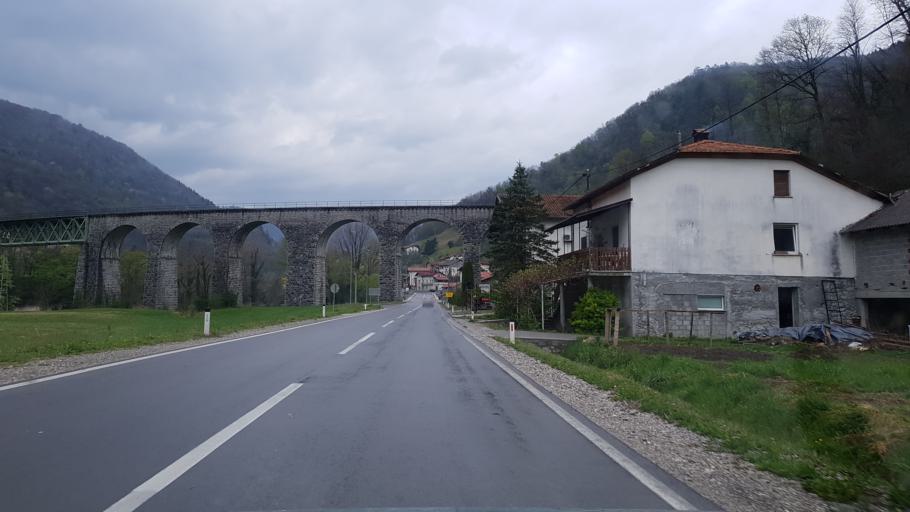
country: SI
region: Tolmin
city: Tolmin
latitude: 46.1440
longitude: 13.7704
